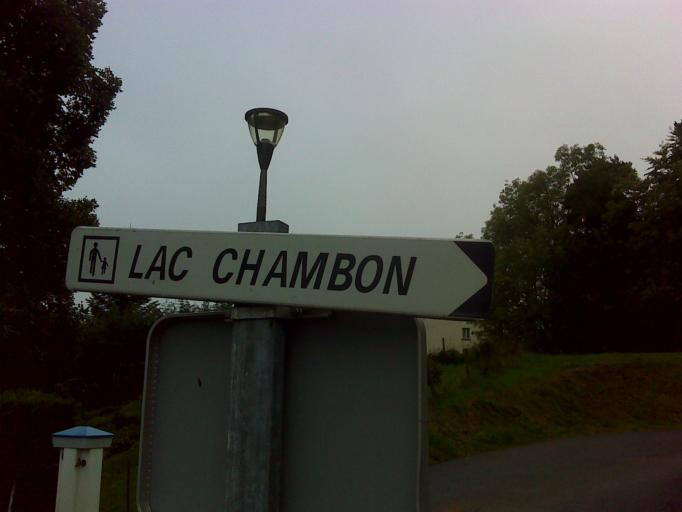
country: FR
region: Auvergne
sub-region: Departement du Puy-de-Dome
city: Aydat
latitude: 45.5725
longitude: 2.9406
